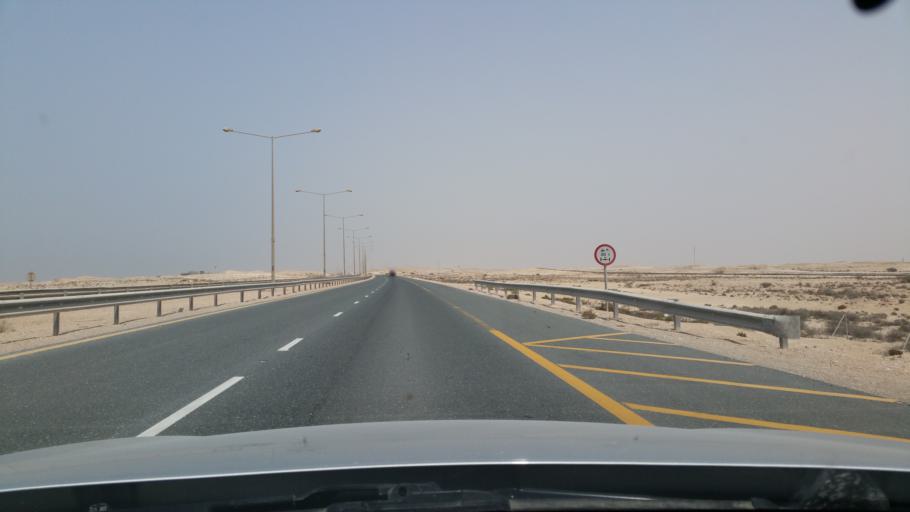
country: QA
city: Umm Bab
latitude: 25.2406
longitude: 50.8011
